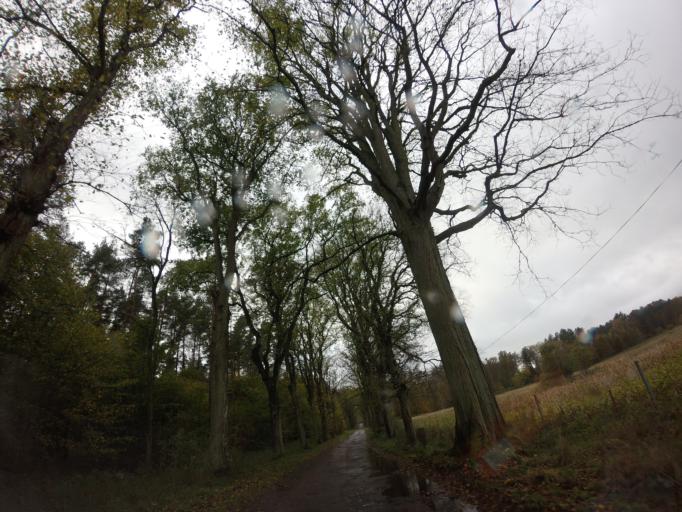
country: PL
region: West Pomeranian Voivodeship
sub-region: Powiat choszczenski
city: Krzecin
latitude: 53.0263
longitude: 15.5301
